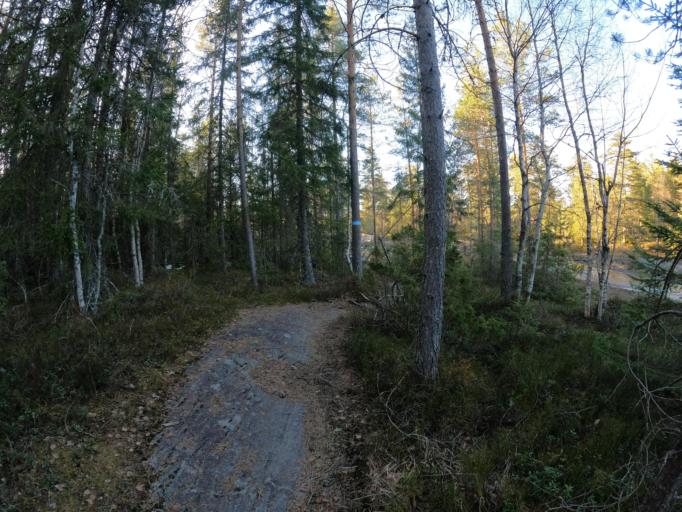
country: NO
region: Akershus
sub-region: Nittedal
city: Aneby
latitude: 60.1068
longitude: 10.9399
